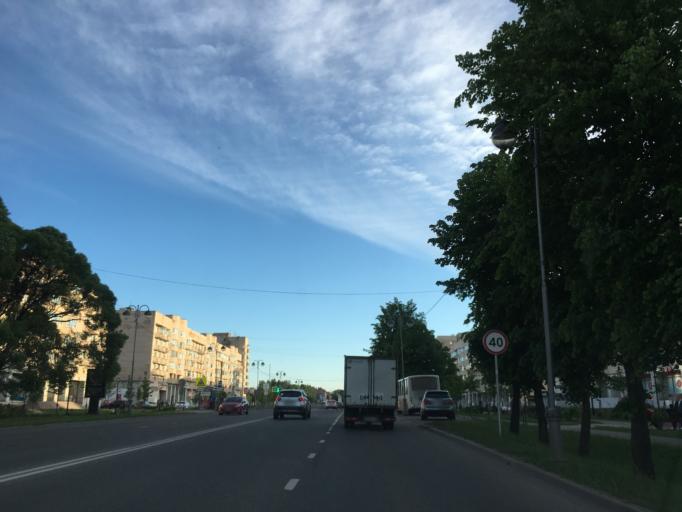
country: RU
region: Leningrad
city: Gatchina
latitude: 59.5792
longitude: 30.1369
